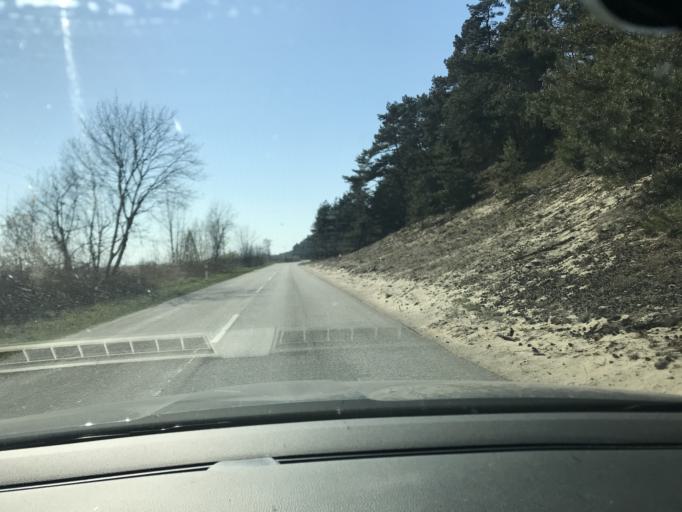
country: PL
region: Pomeranian Voivodeship
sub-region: Powiat nowodworski
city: Sztutowo
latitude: 54.3502
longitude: 19.2775
